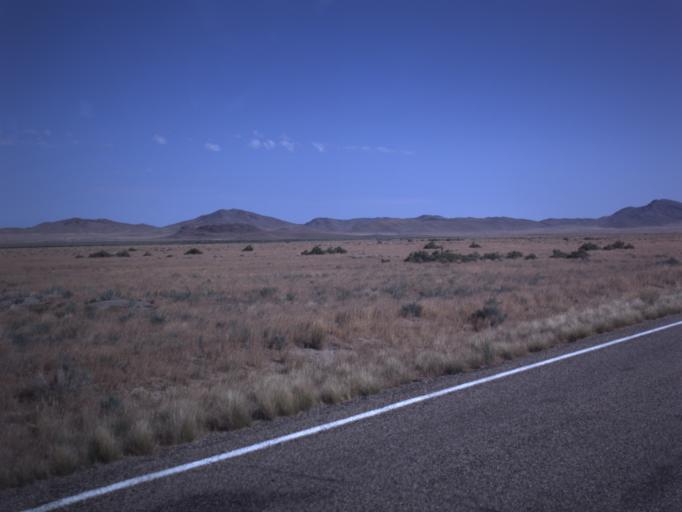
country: US
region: Utah
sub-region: Beaver County
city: Milford
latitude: 38.6530
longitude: -112.9822
